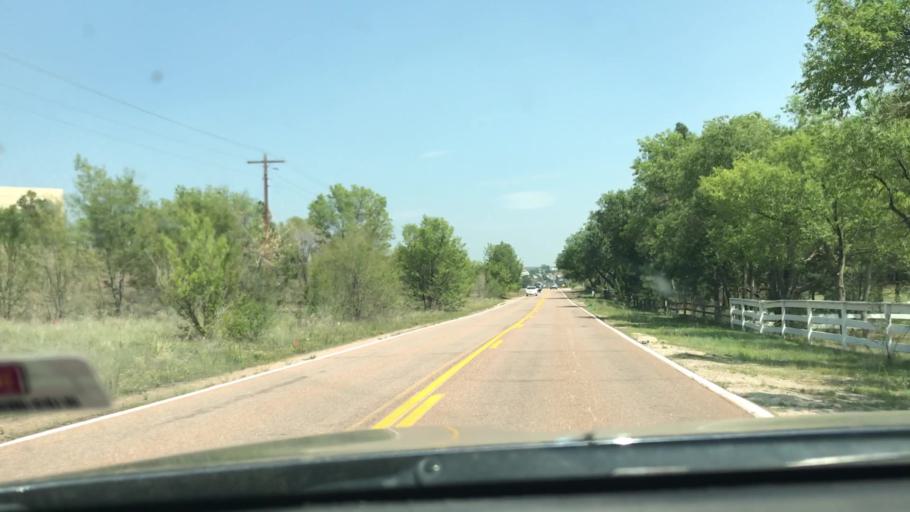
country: US
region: Colorado
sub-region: El Paso County
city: Gleneagle
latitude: 38.9805
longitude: -104.7930
